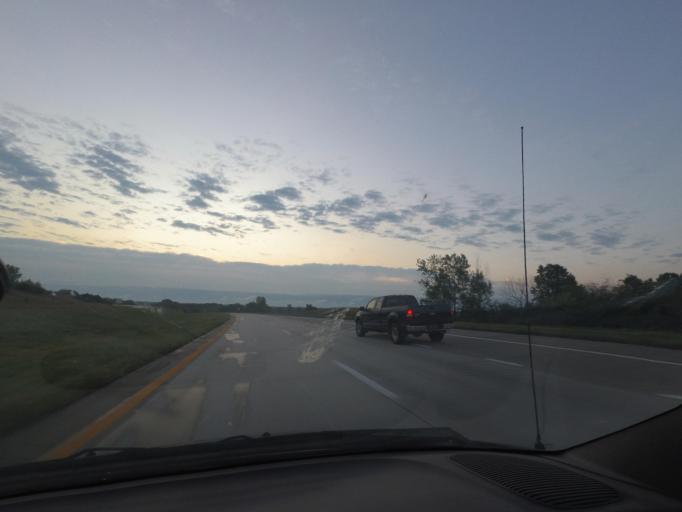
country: US
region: Missouri
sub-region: Macon County
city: Macon
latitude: 39.7539
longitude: -92.6181
